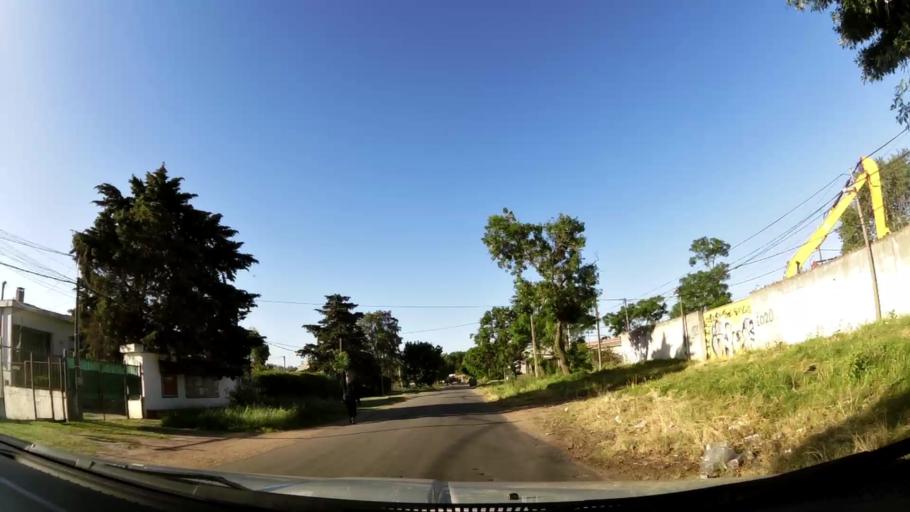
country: UY
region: Canelones
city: La Paz
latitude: -34.8340
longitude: -56.2407
